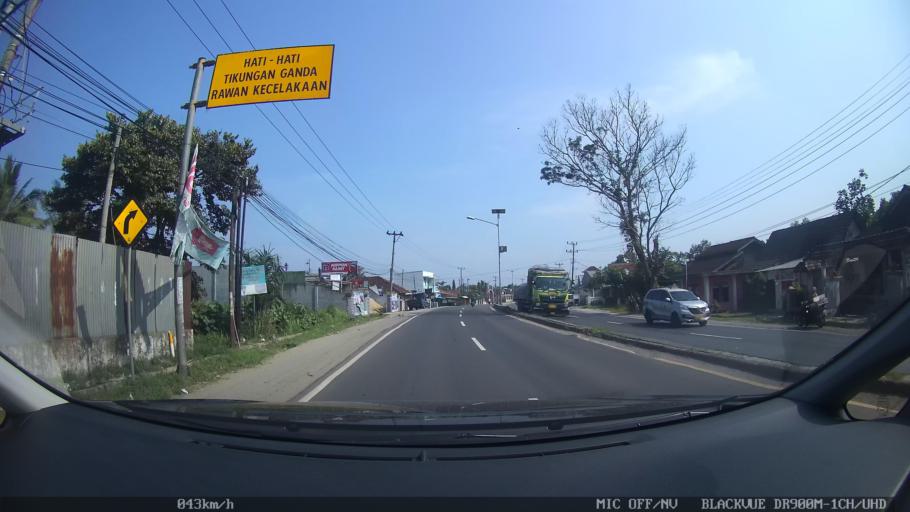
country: ID
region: Lampung
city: Natar
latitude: -5.2629
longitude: 105.1848
